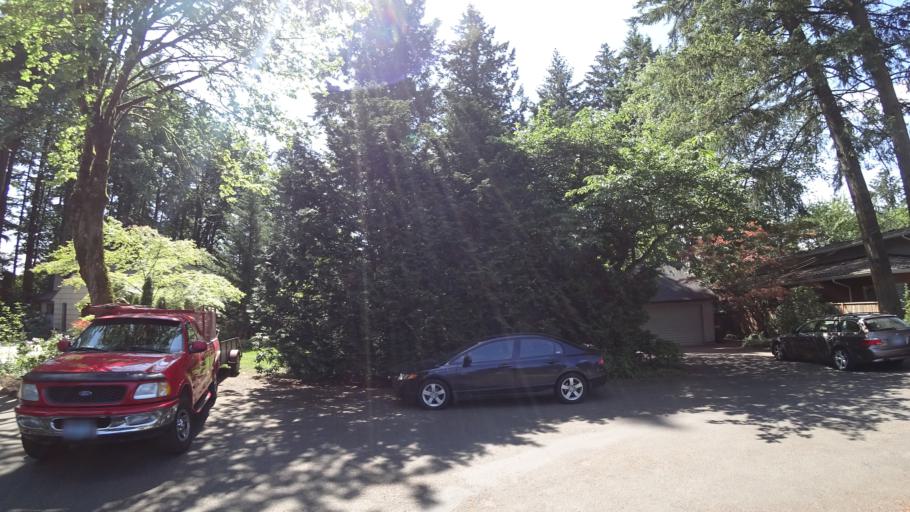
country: US
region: Oregon
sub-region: Clackamas County
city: Lake Oswego
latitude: 45.4293
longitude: -122.7017
